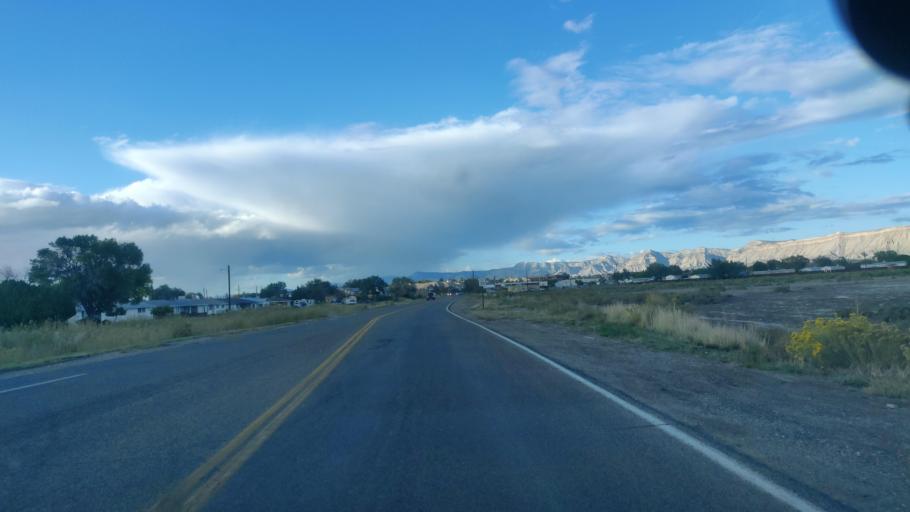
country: US
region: Colorado
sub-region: Mesa County
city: Grand Junction
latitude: 39.0708
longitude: -108.5336
